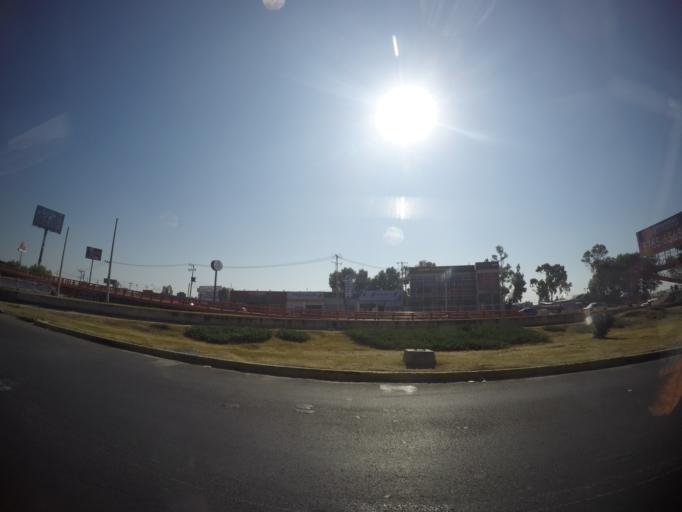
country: MX
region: Mexico
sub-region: Atenco
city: Colonia el Salado
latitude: 19.6021
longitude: -99.0156
